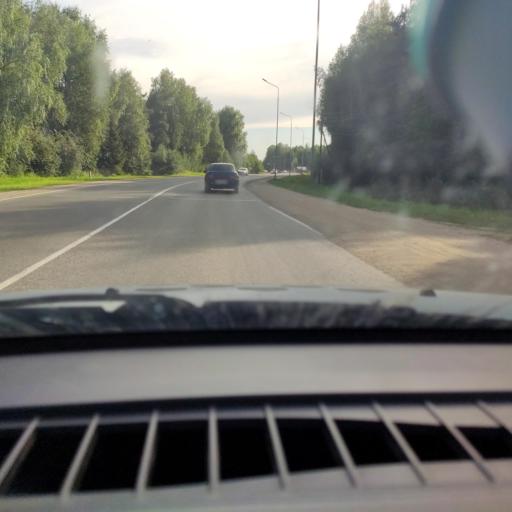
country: RU
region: Kirov
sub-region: Kirovo-Chepetskiy Rayon
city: Kirov
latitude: 58.6228
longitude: 49.7804
